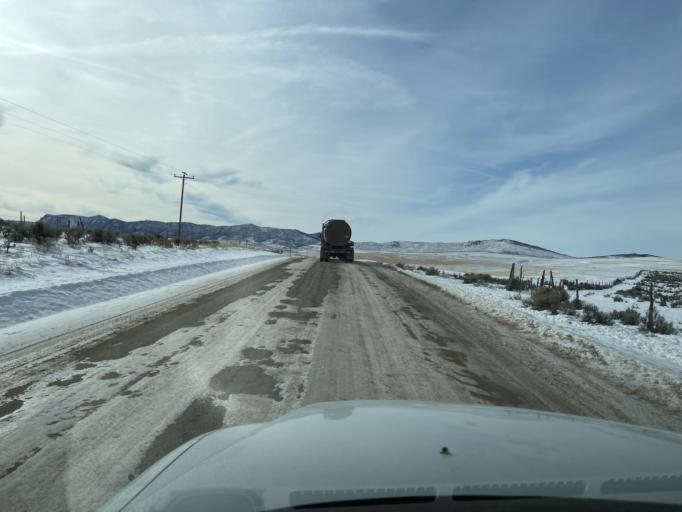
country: US
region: Colorado
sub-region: Moffat County
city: Craig
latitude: 40.3174
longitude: -107.6915
